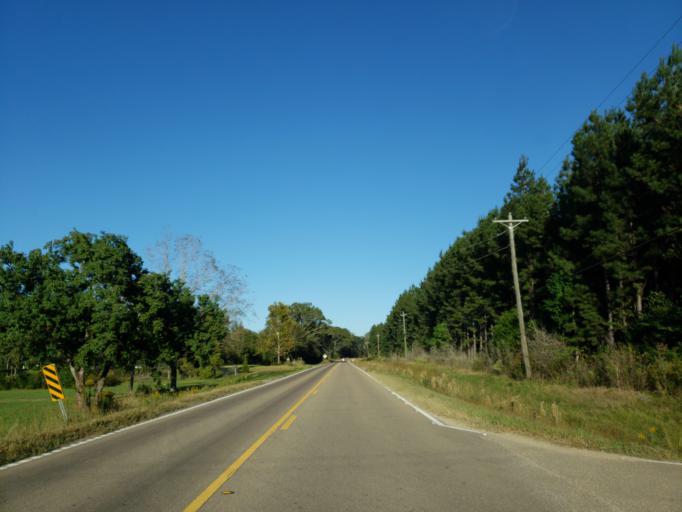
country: US
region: Mississippi
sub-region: Perry County
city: Richton
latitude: 31.3728
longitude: -88.8664
